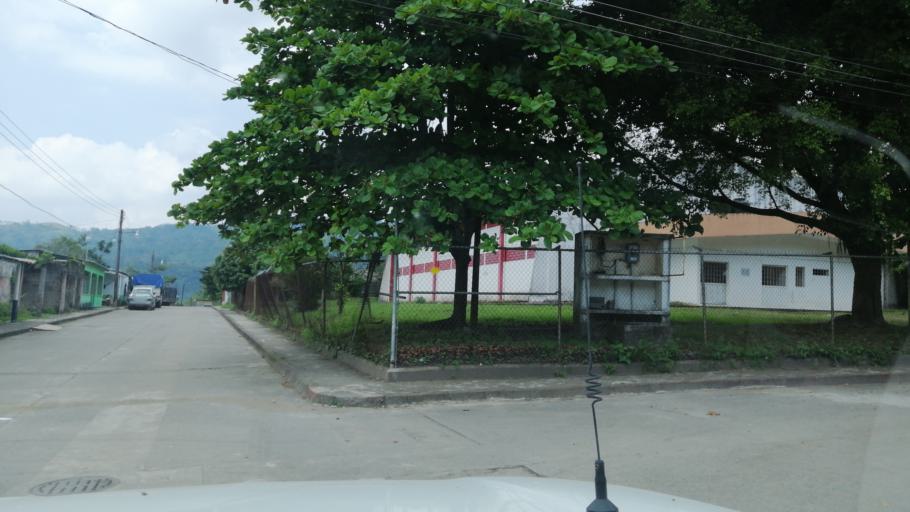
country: MX
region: Chiapas
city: Ostuacan
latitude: 17.4082
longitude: -93.3379
